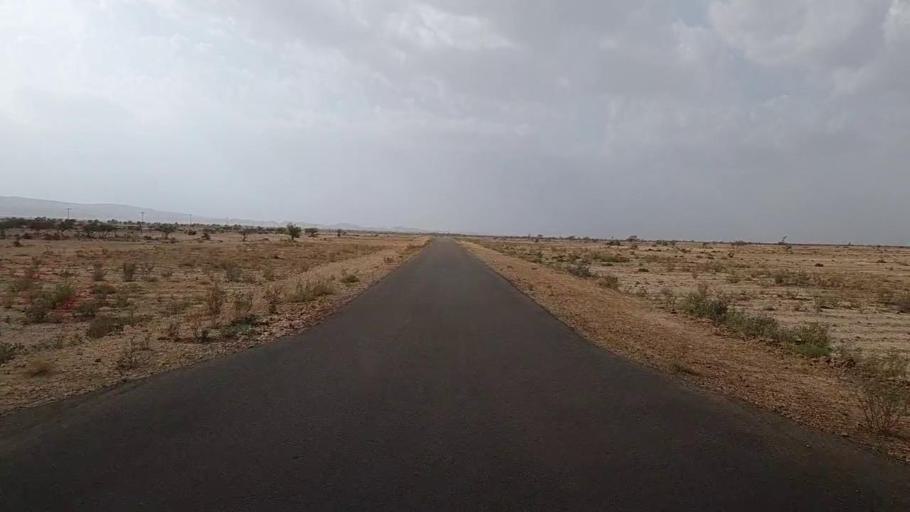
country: PK
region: Sindh
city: Jamshoro
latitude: 25.4401
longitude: 67.6836
